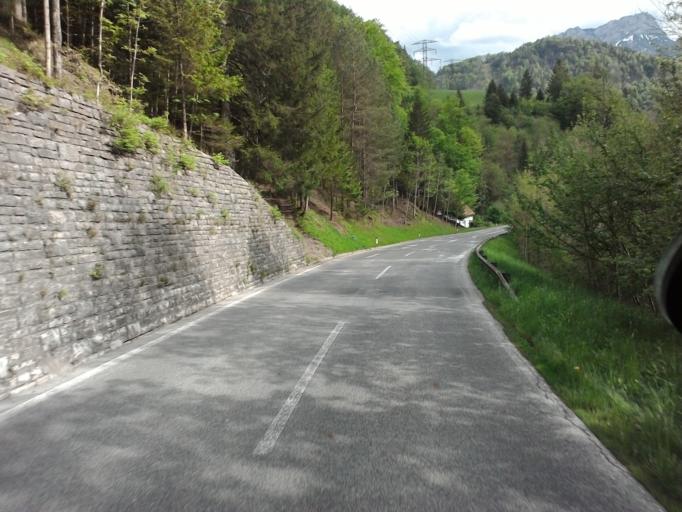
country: AT
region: Styria
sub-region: Politischer Bezirk Liezen
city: Landl
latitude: 47.6735
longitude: 14.7134
